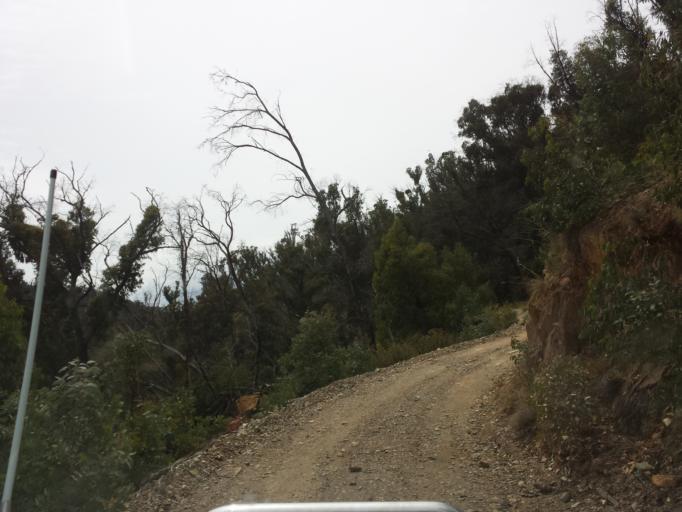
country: AU
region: Victoria
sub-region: Wellington
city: Heyfield
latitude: -37.7549
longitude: 146.5147
